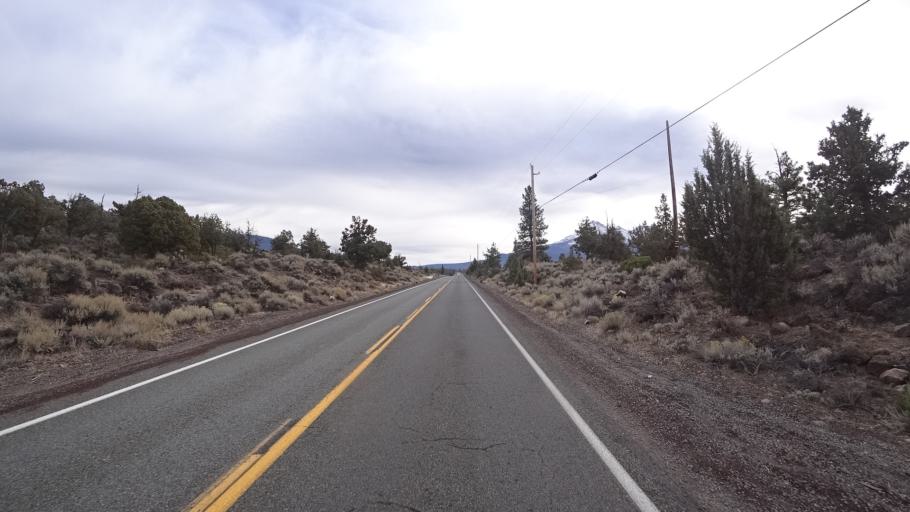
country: US
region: California
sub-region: Siskiyou County
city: Weed
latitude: 41.5592
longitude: -122.2582
